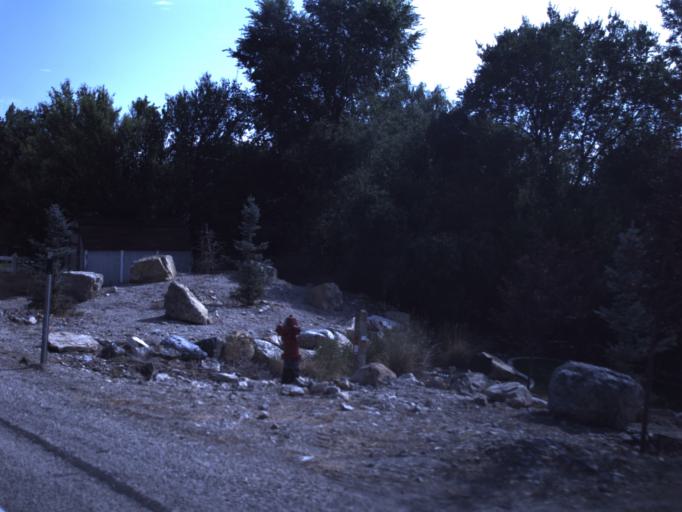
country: US
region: Utah
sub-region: Box Elder County
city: Brigham City
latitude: 41.5627
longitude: -112.0239
